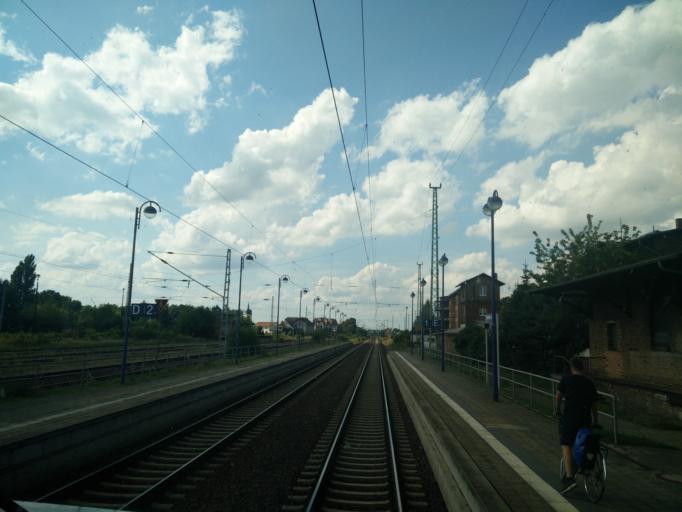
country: DE
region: Brandenburg
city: Lubbenau
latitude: 51.8623
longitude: 13.9607
